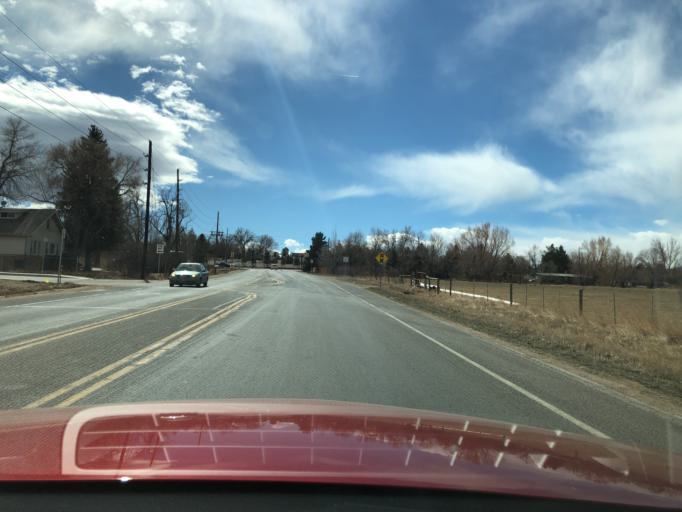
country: US
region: Colorado
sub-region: Boulder County
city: Superior
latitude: 40.0021
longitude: -105.1783
